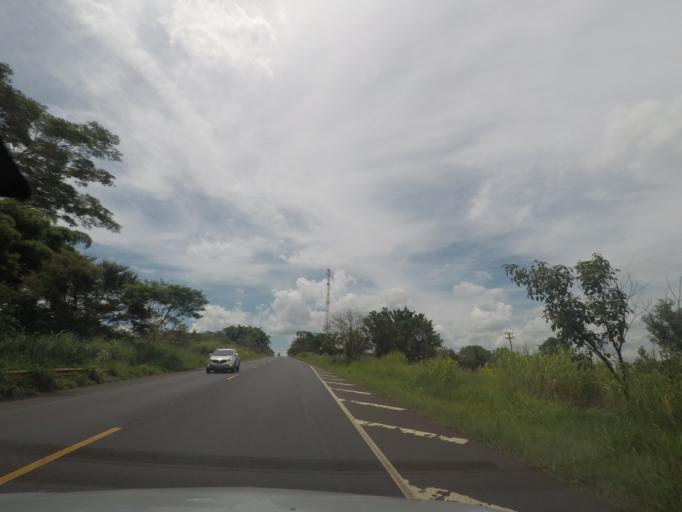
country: BR
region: Sao Paulo
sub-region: Barretos
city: Barretos
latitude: -20.4246
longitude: -48.6295
